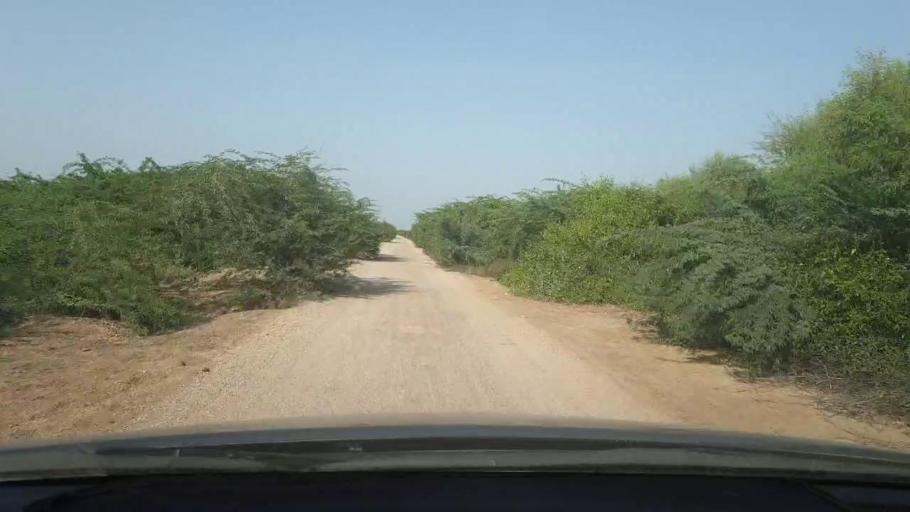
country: PK
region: Sindh
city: Naukot
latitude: 24.7794
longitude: 69.2908
